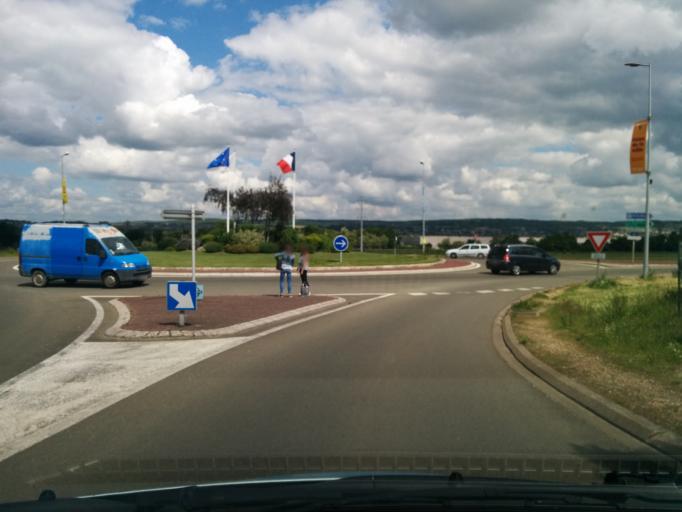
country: FR
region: Ile-de-France
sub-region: Departement des Yvelines
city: Aubergenville
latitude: 48.9592
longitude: 1.8410
